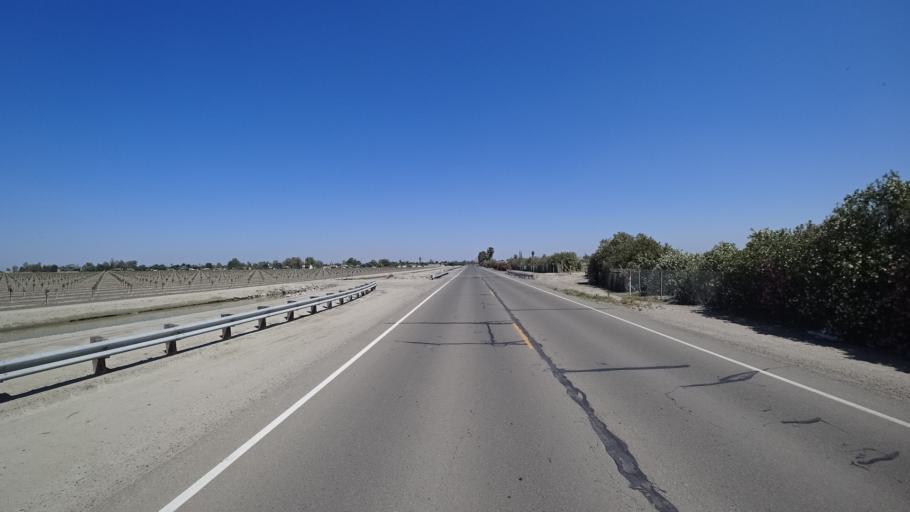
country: US
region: California
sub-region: Kings County
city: Corcoran
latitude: 36.0758
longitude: -119.5586
